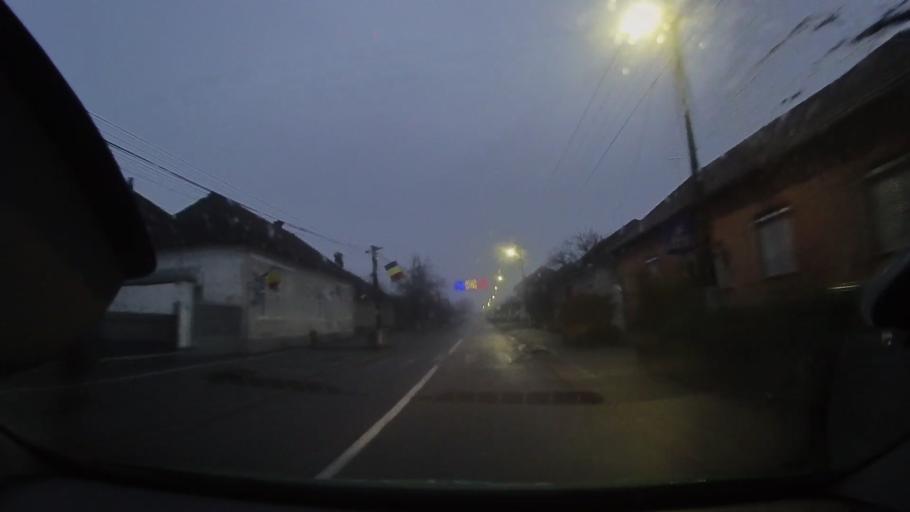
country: RO
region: Arad
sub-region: Comuna Archis
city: Archis
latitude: 46.4772
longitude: 22.0532
